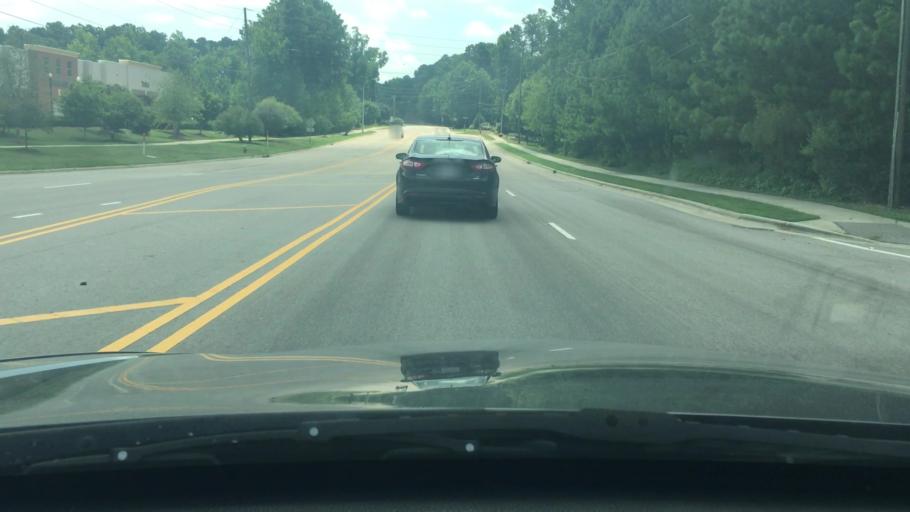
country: US
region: North Carolina
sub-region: Wake County
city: Cary
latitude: 35.7977
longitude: -78.7948
